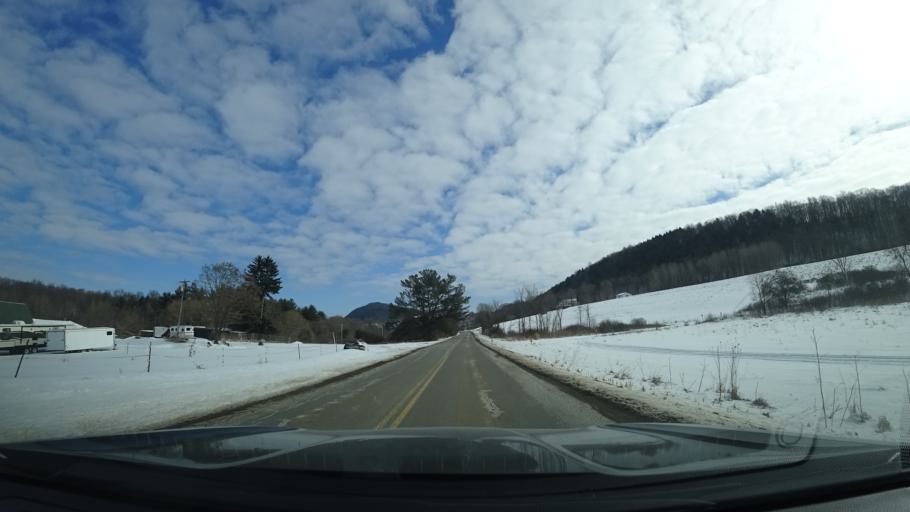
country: US
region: New York
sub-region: Washington County
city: Fort Edward
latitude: 43.2442
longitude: -73.4720
